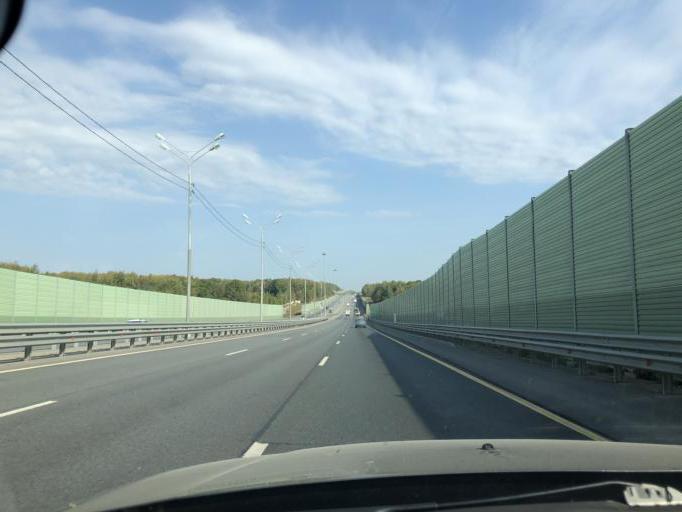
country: RU
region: Moskovskaya
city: Danki
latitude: 54.9477
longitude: 37.5302
